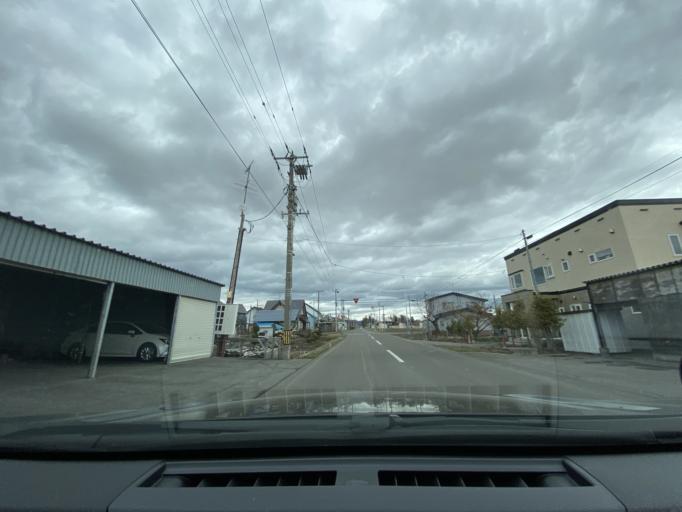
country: JP
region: Hokkaido
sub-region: Asahikawa-shi
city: Asahikawa
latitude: 43.8683
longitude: 142.4757
